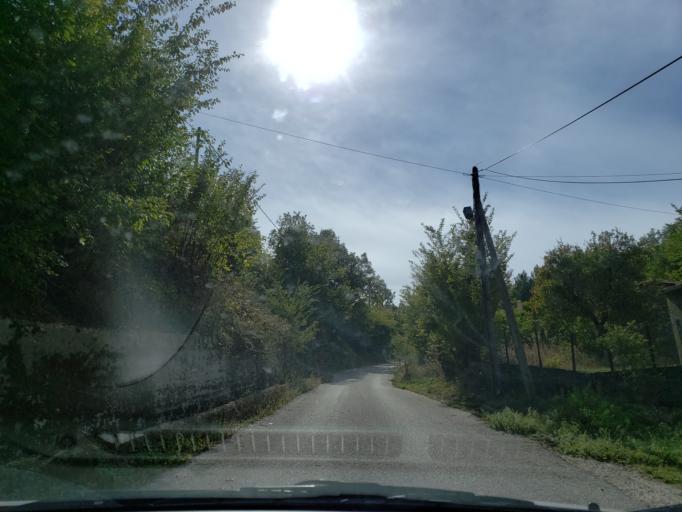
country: GR
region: Thessaly
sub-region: Trikala
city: Kastraki
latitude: 39.7735
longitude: 21.6584
